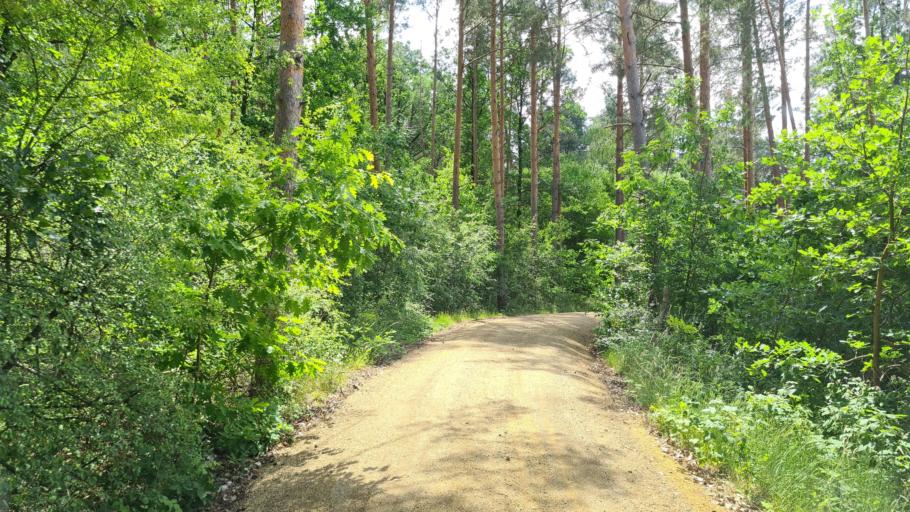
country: DE
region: Brandenburg
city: Plessa
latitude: 51.4935
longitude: 13.6219
